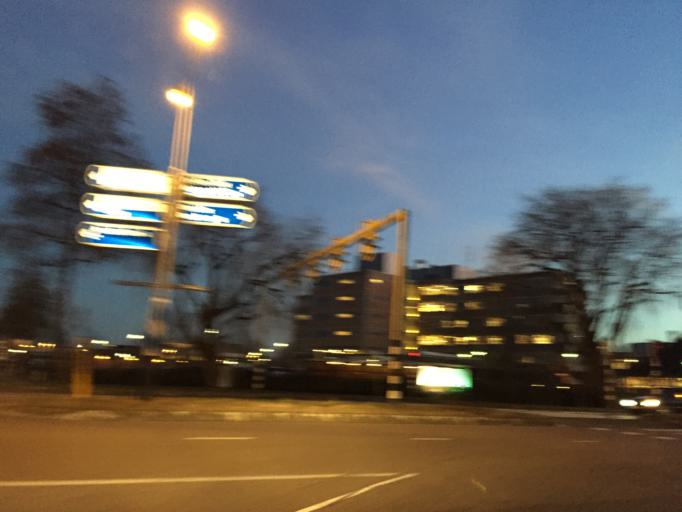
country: NL
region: South Holland
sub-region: Gemeente Leiderdorp
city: Leiderdorp
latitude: 52.1568
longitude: 4.5360
